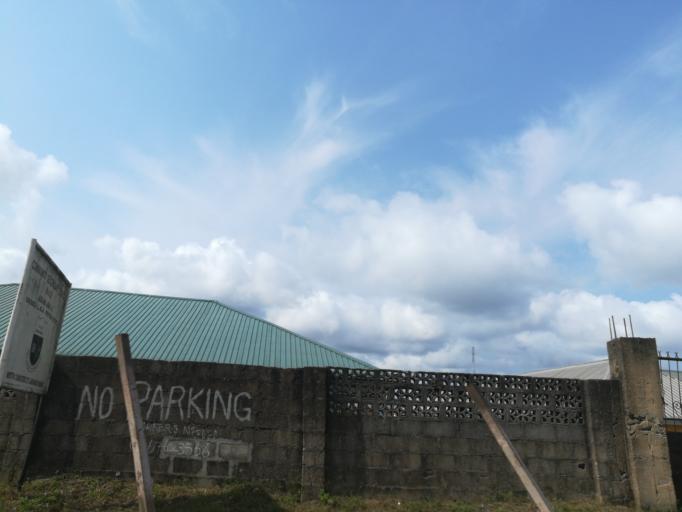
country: NG
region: Rivers
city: Okrika
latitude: 4.7642
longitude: 7.0860
